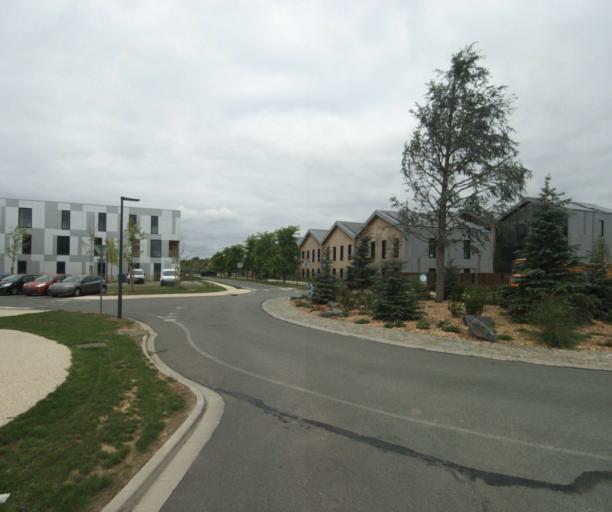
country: FR
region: Nord-Pas-de-Calais
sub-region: Departement du Nord
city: Lesquin
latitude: 50.5953
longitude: 3.1309
